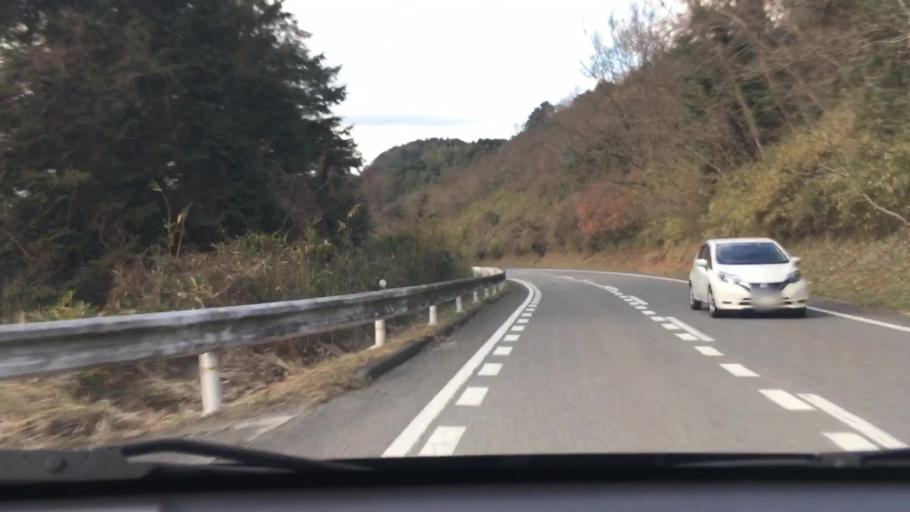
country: JP
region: Oita
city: Hiji
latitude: 33.4109
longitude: 131.4252
